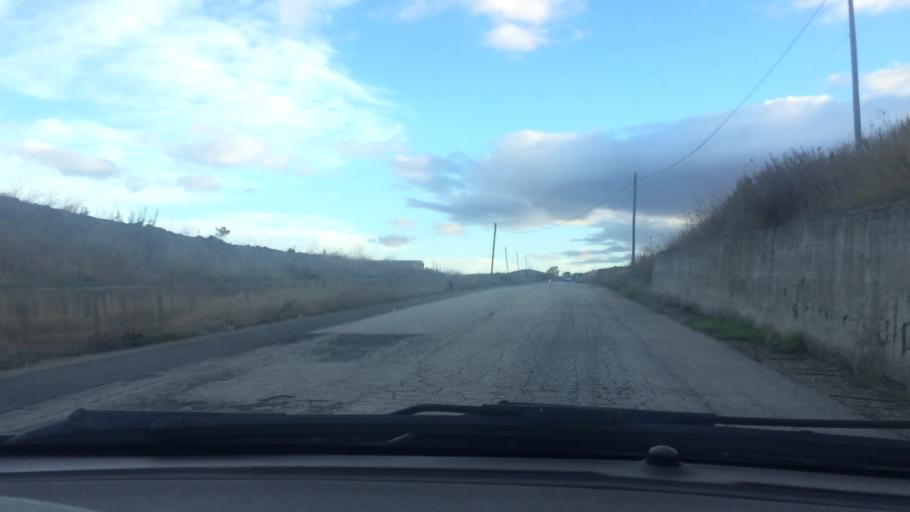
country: IT
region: Basilicate
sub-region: Provincia di Potenza
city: Tolve
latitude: 40.7072
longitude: 16.0164
